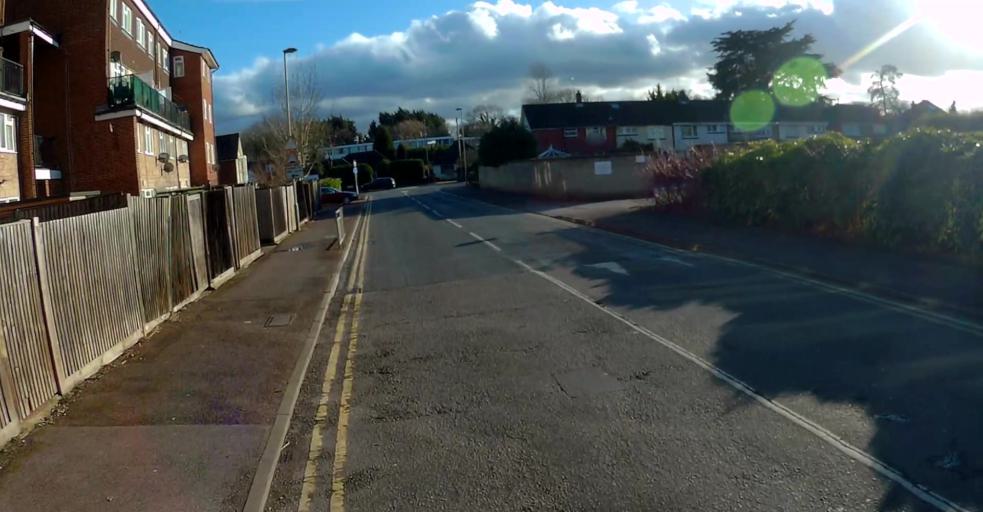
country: GB
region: England
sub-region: Surrey
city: Addlestone
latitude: 51.3688
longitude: -0.4892
